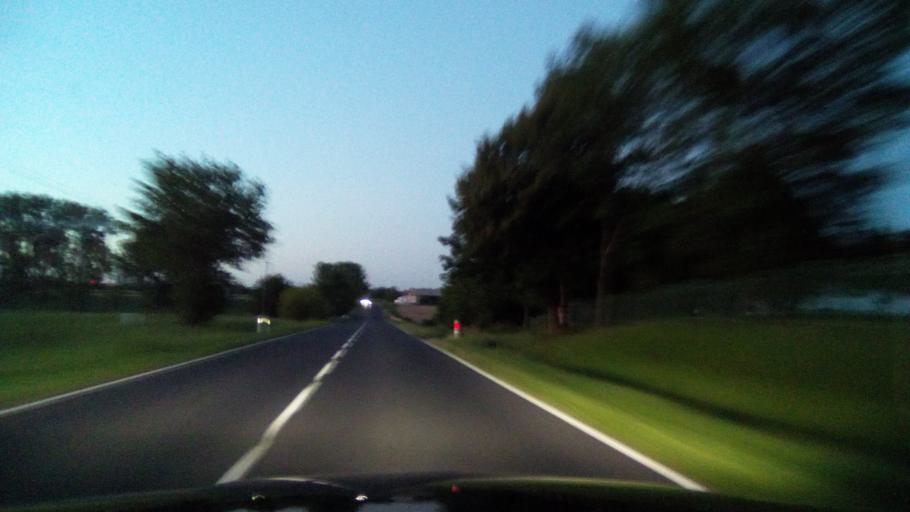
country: PL
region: Greater Poland Voivodeship
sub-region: Powiat koninski
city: Golina
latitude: 52.2341
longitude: 18.0755
